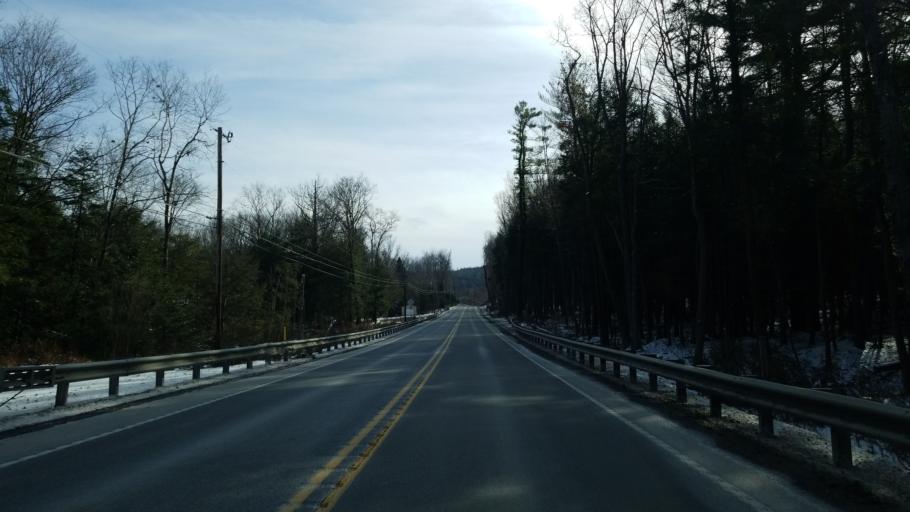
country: US
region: Pennsylvania
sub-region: Clearfield County
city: Treasure Lake
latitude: 41.1723
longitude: -78.5511
